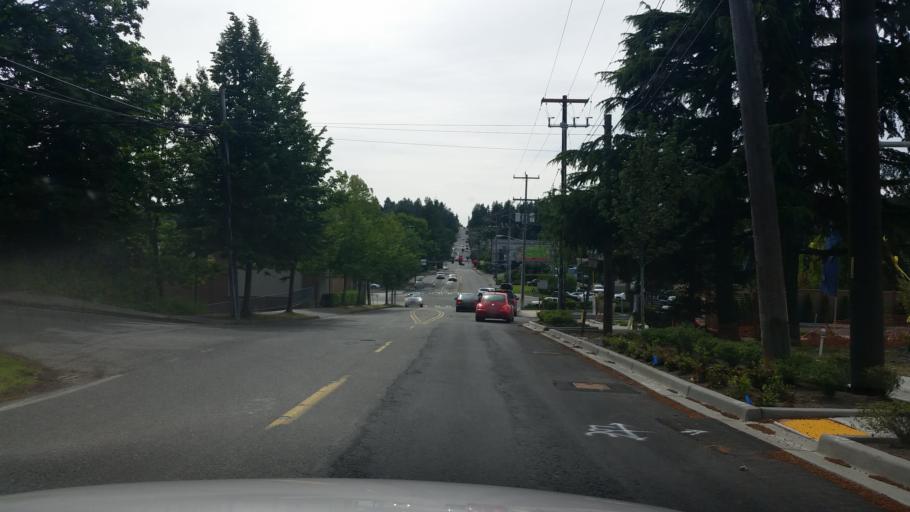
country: US
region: Washington
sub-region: King County
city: Lake Forest Park
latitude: 47.7338
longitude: -122.2909
